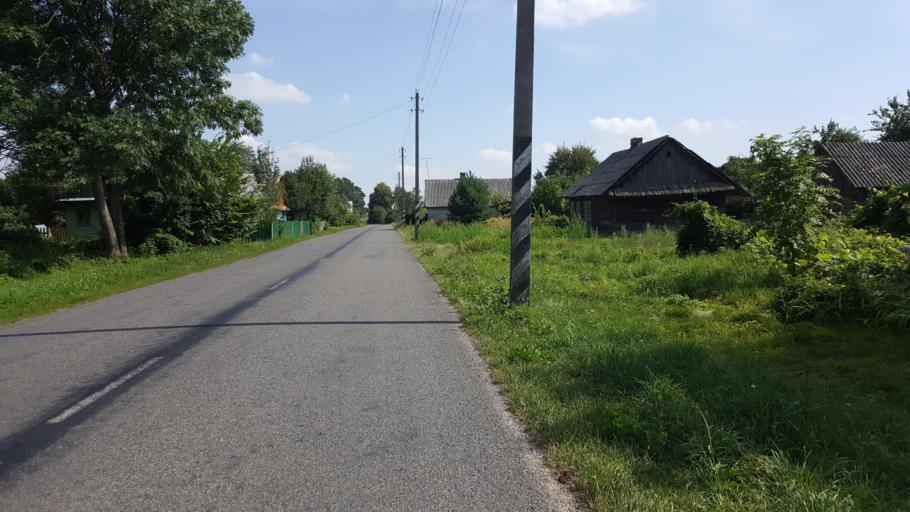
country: BY
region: Brest
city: Kamyanyuki
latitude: 52.5053
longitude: 23.6544
